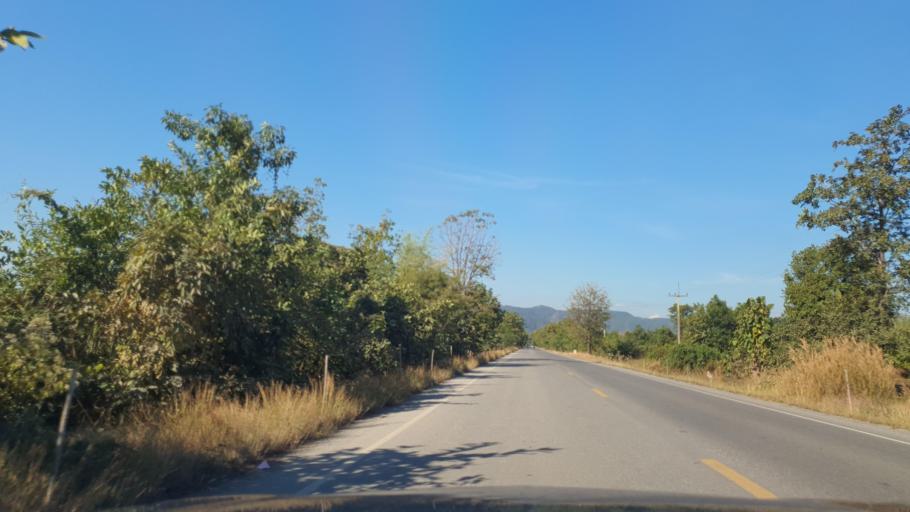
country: TH
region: Sukhothai
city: Thung Saliam
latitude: 17.2026
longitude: 99.5425
